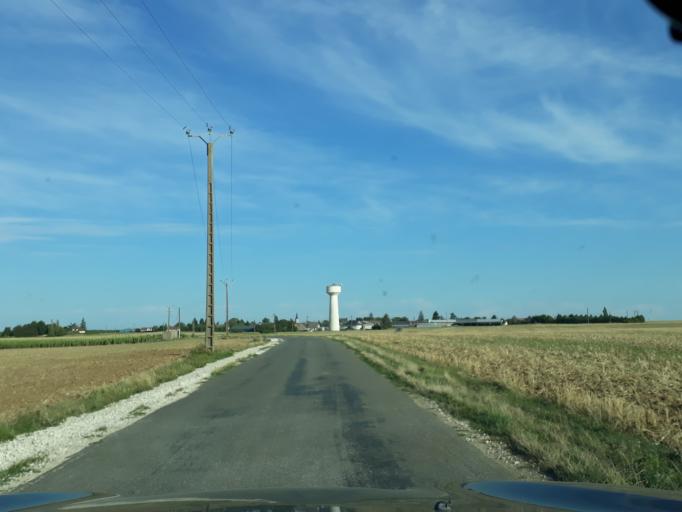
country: FR
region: Centre
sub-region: Departement du Loir-et-Cher
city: Ouzouer-le-Marche
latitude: 47.9325
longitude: 1.5675
